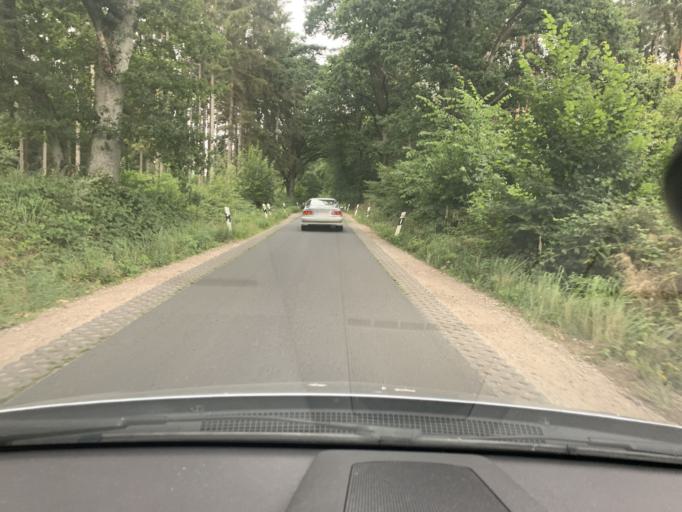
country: DE
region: Schleswig-Holstein
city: Guster
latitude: 53.5583
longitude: 10.6935
